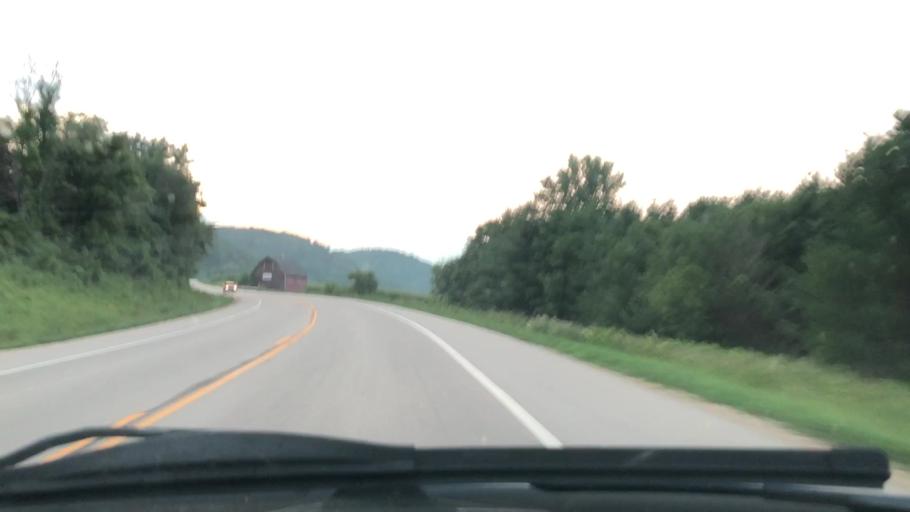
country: US
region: Wisconsin
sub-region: Richland County
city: Richland Center
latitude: 43.3490
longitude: -90.5452
